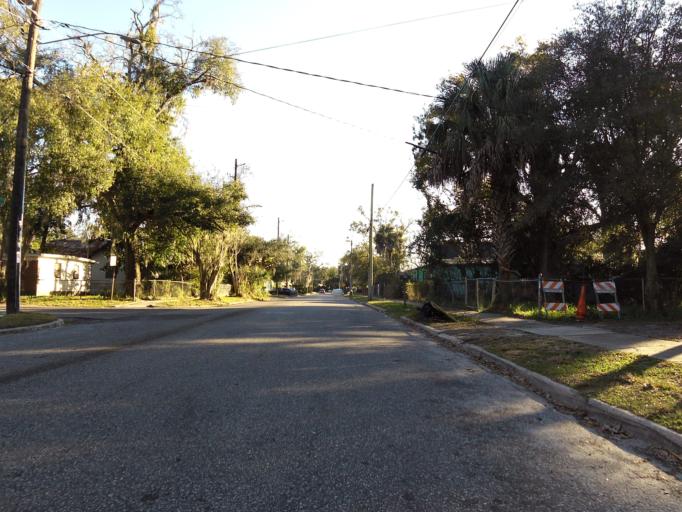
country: US
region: Florida
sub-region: Duval County
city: Jacksonville
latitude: 30.3245
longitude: -81.6967
